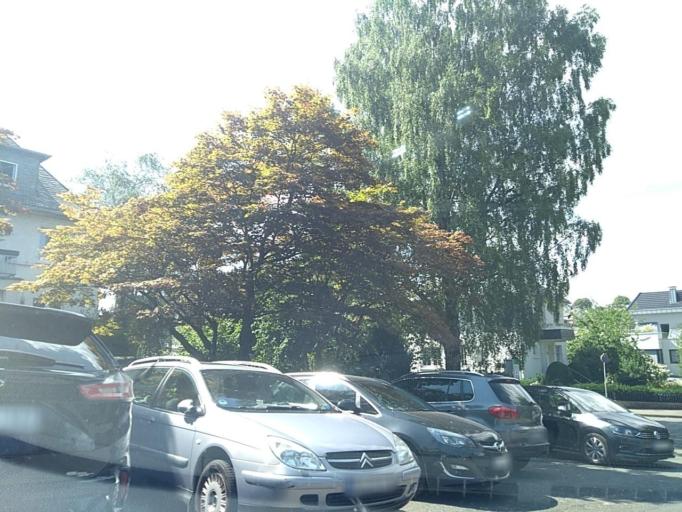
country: DE
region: North Rhine-Westphalia
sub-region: Regierungsbezirk Arnsberg
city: Brilon
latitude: 51.3922
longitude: 8.5754
